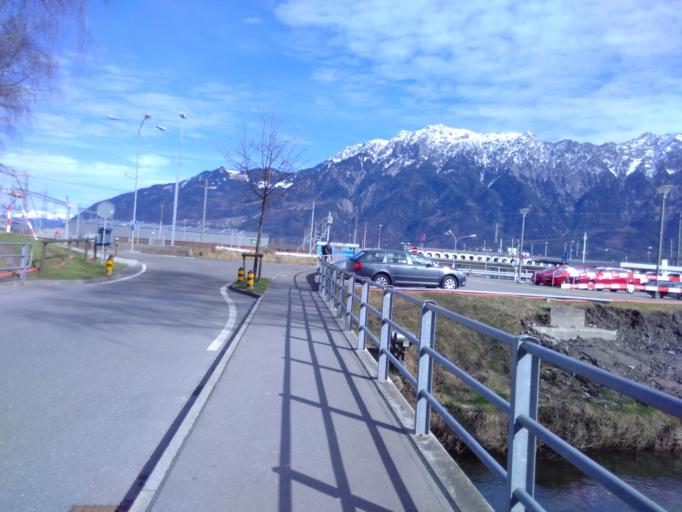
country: CH
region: Saint Gallen
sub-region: Wahlkreis Werdenberg
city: Buchs
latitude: 47.1695
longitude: 9.4770
